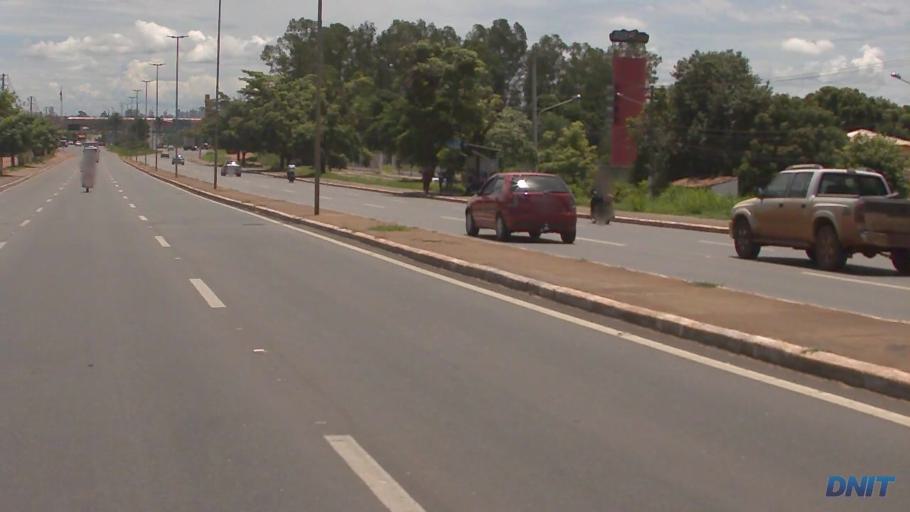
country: BR
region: Mato Grosso
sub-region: Cuiaba
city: Cuiaba
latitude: -15.6432
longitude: -56.0166
